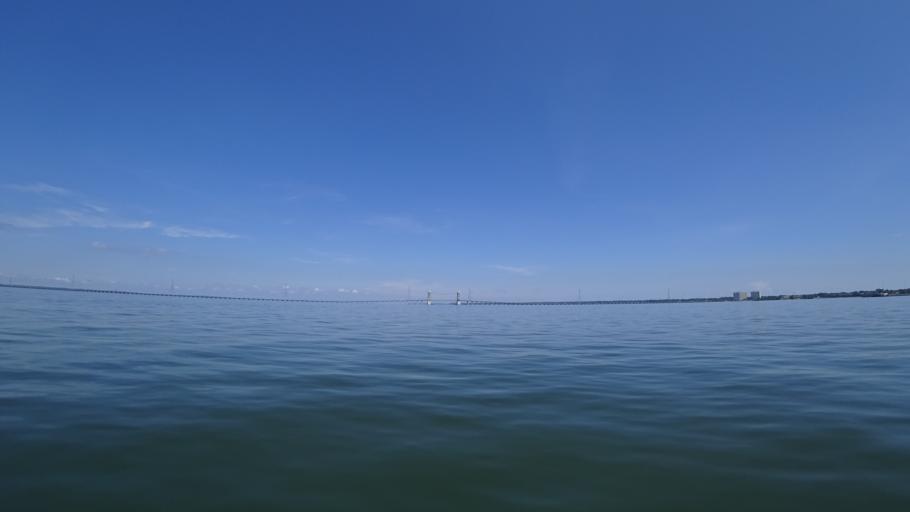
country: US
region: Virginia
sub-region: City of Newport News
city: Newport News
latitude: 36.9907
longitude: -76.4568
